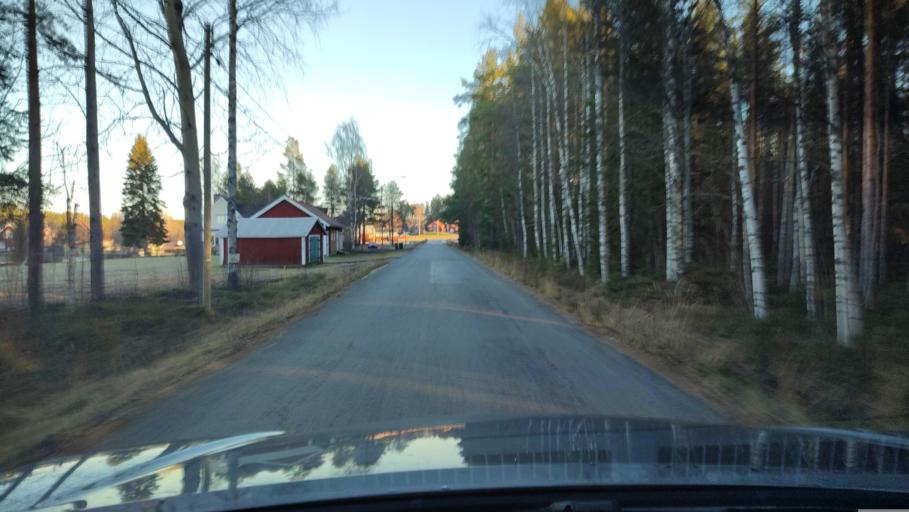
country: SE
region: Vaesterbotten
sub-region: Skelleftea Kommun
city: Soedra Bergsbyn
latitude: 64.6308
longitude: 21.0589
